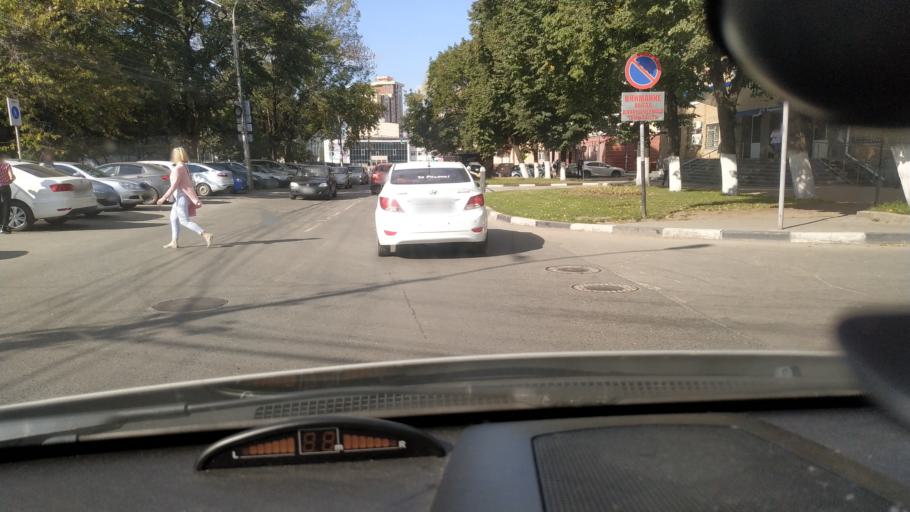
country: RU
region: Rjazan
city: Ryazan'
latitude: 54.6274
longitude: 39.7113
